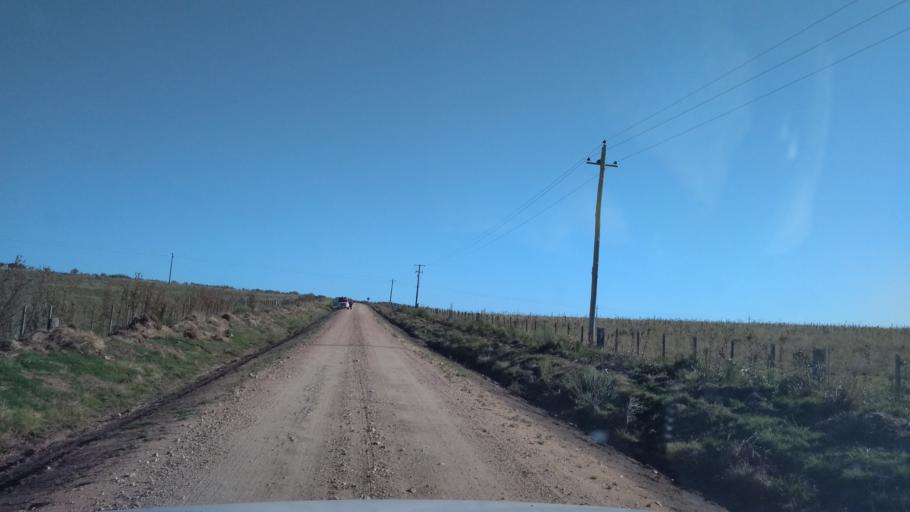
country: UY
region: Florida
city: Casupa
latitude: -34.0028
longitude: -55.7876
